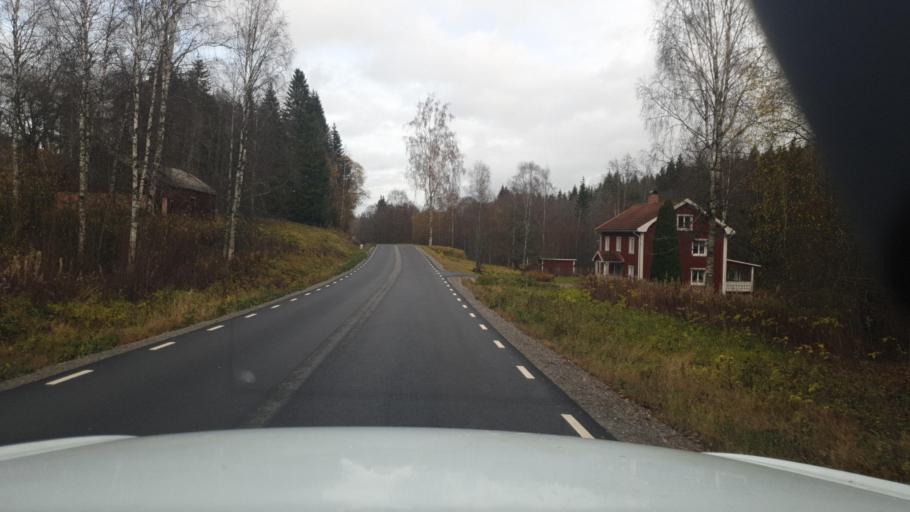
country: SE
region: Vaermland
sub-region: Torsby Kommun
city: Torsby
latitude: 59.9798
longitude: 12.8152
